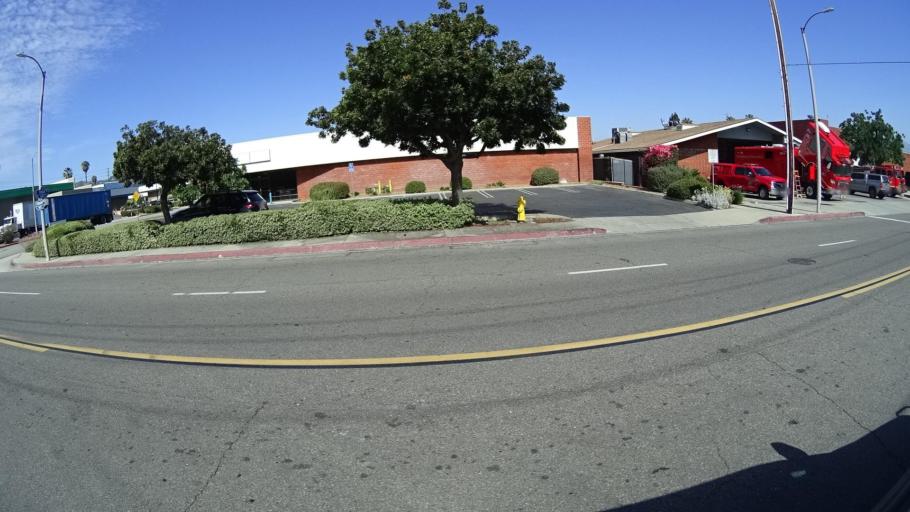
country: US
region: California
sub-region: Los Angeles County
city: La Puente
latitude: 34.0100
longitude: -117.9555
